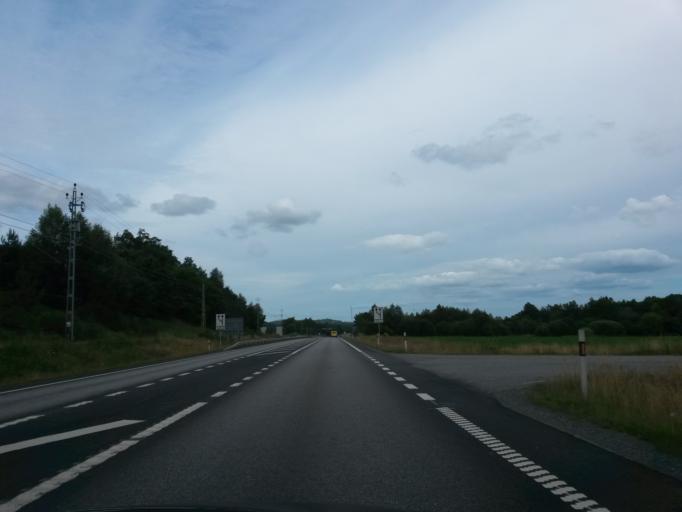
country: SE
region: Vaestra Goetaland
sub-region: Marks Kommun
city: Kinna
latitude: 57.4619
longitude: 12.5920
